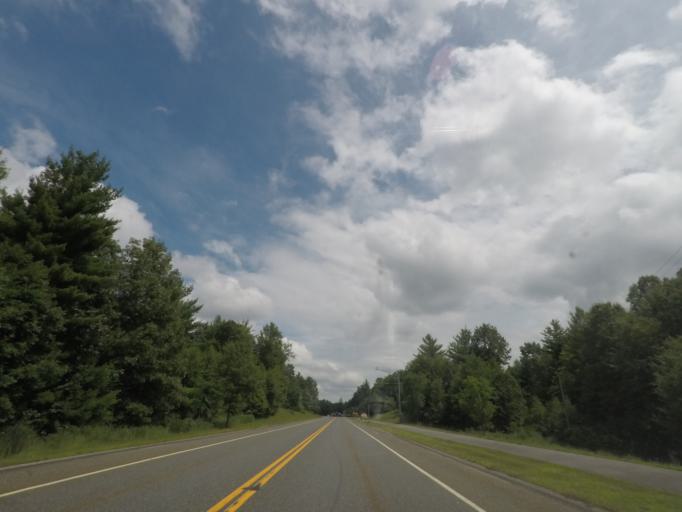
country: US
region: New York
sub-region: Saratoga County
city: Country Knolls
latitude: 42.9566
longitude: -73.7496
